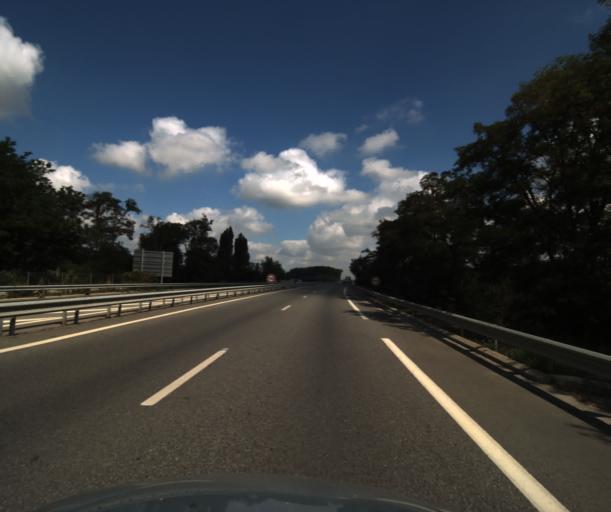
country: FR
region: Midi-Pyrenees
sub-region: Departement de la Haute-Garonne
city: Labarthe-sur-Leze
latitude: 43.4593
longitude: 1.4149
